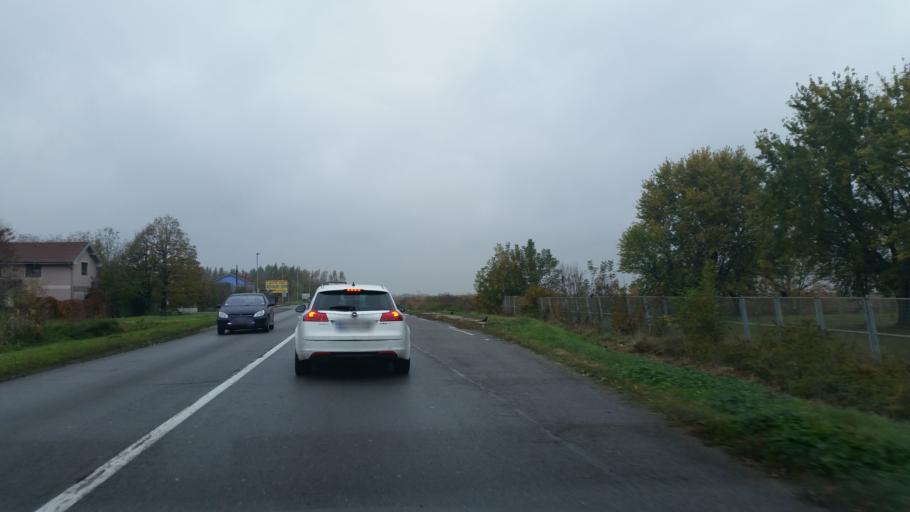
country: RS
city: Sefkerin
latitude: 44.9328
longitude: 20.4376
